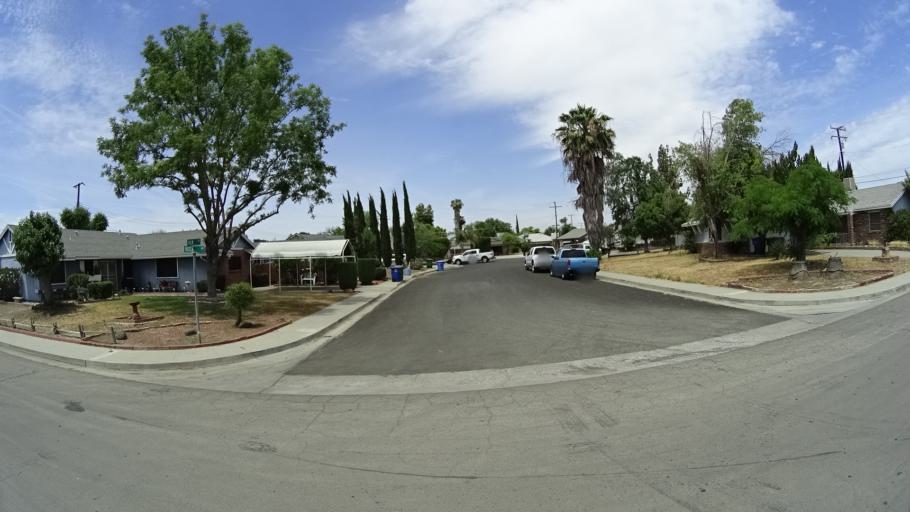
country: US
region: California
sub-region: Kings County
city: Armona
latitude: 36.3091
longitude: -119.7112
